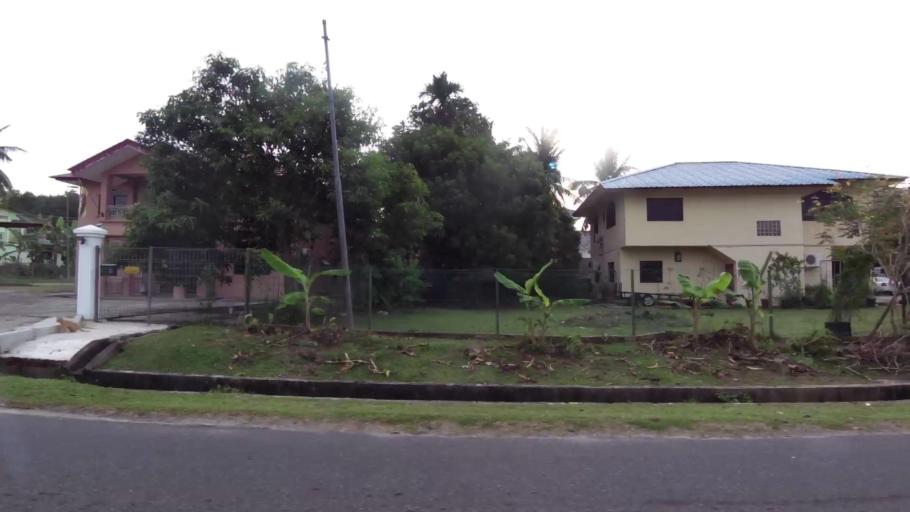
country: BN
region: Brunei and Muara
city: Bandar Seri Begawan
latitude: 4.9101
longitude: 114.8944
